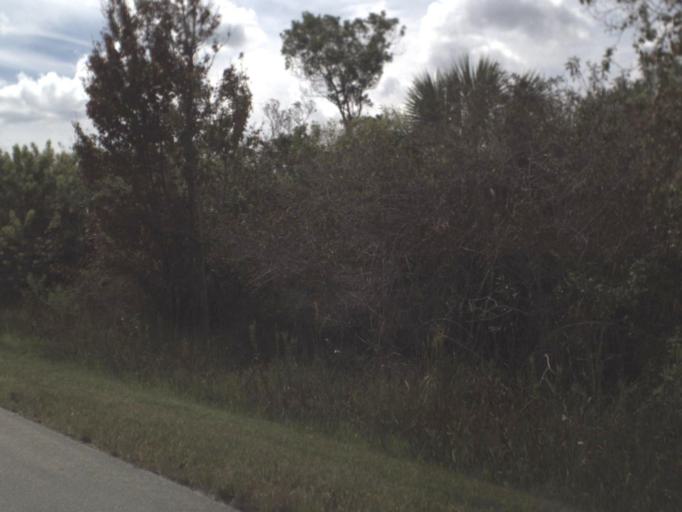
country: US
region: Florida
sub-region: Collier County
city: Lely Resort
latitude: 25.9311
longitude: -81.3575
